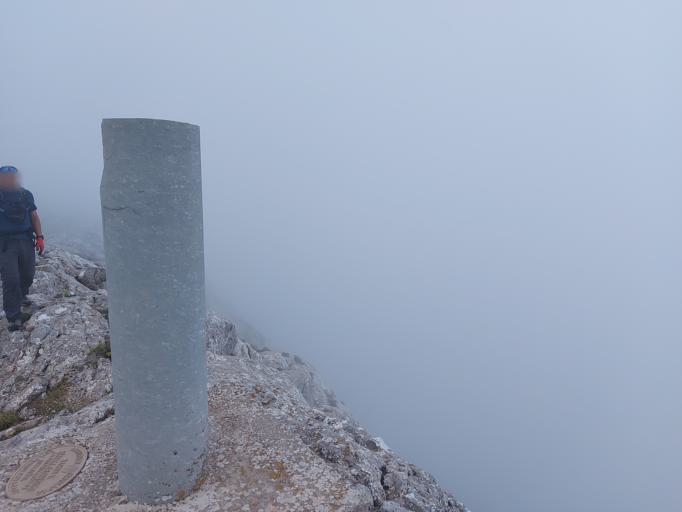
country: ES
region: Balearic Islands
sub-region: Illes Balears
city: Fornalutx
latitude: 39.8105
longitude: 2.7979
